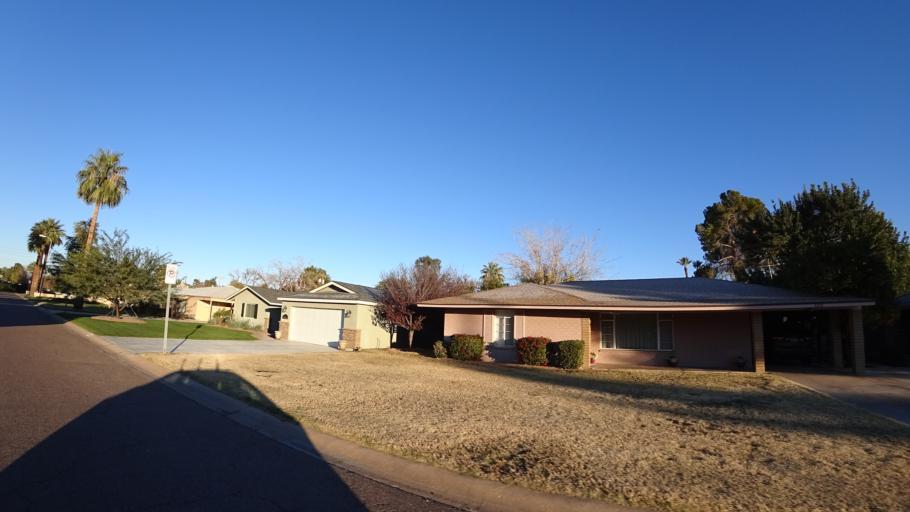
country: US
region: Arizona
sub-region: Maricopa County
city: Paradise Valley
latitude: 33.4816
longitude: -111.9897
